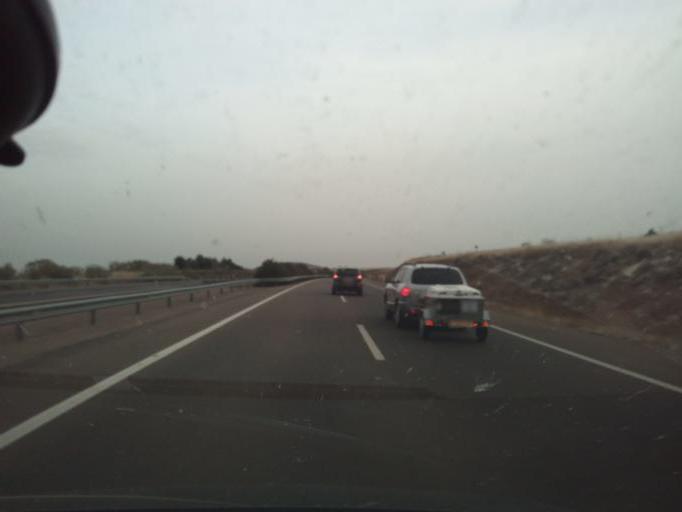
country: ES
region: Extremadura
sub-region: Provincia de Badajoz
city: Merida
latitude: 38.9449
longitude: -6.3083
